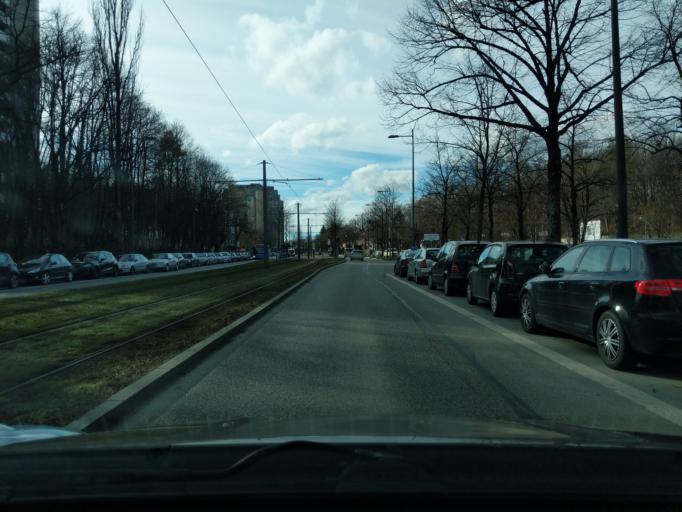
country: DE
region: Bavaria
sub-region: Upper Bavaria
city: Bogenhausen
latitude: 48.1537
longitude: 11.6252
